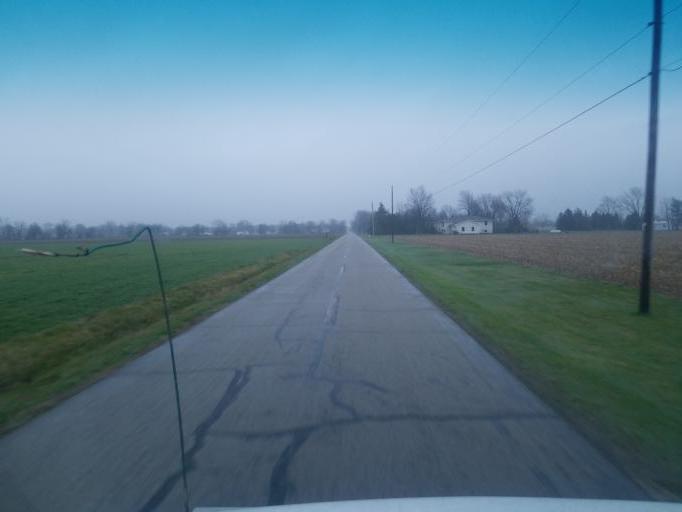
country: US
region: Ohio
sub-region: Henry County
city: Napoleon
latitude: 41.4135
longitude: -84.1978
